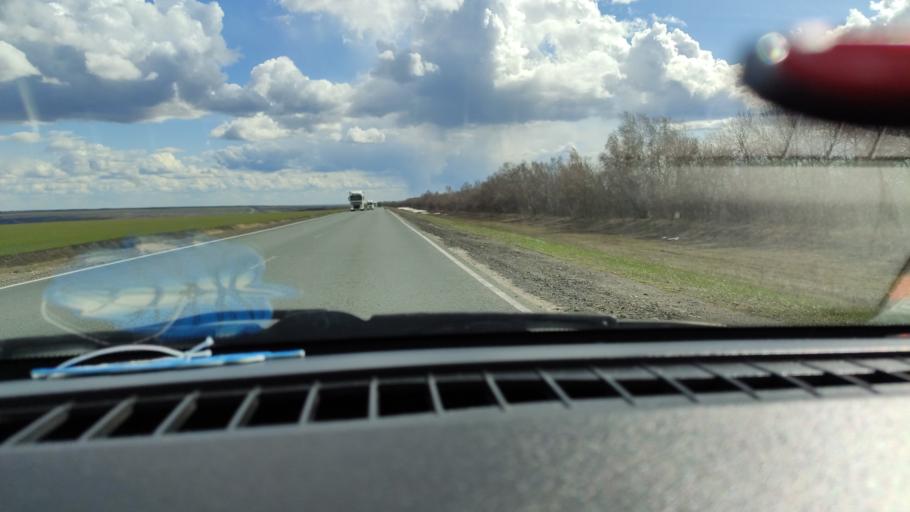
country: RU
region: Saratov
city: Dukhovnitskoye
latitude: 52.7698
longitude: 48.2368
